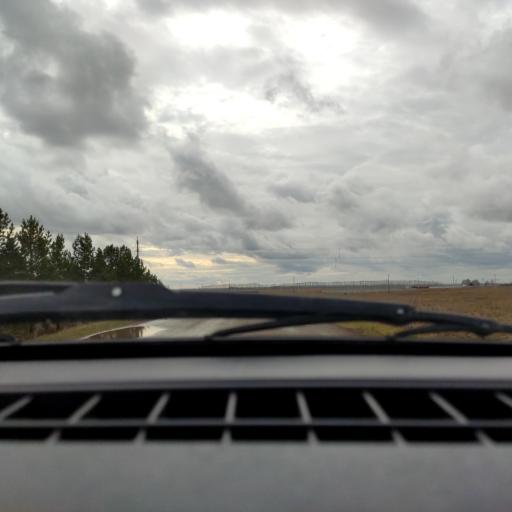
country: RU
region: Bashkortostan
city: Asanovo
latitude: 54.9603
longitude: 55.5378
